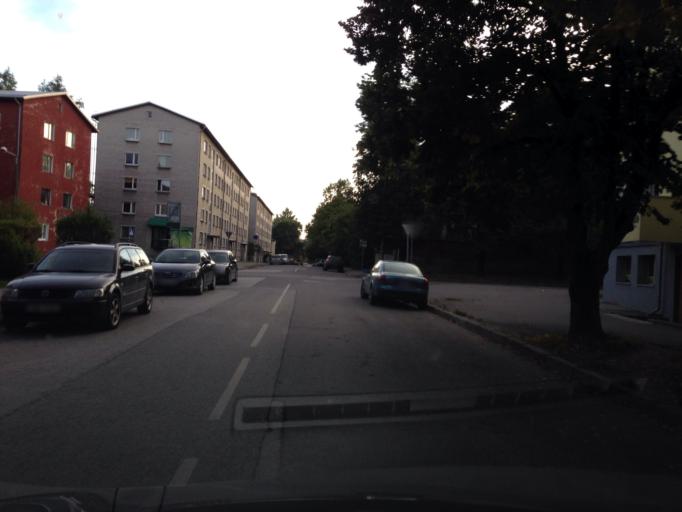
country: EE
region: Tartu
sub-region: Tartu linn
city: Tartu
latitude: 58.3764
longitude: 26.7181
